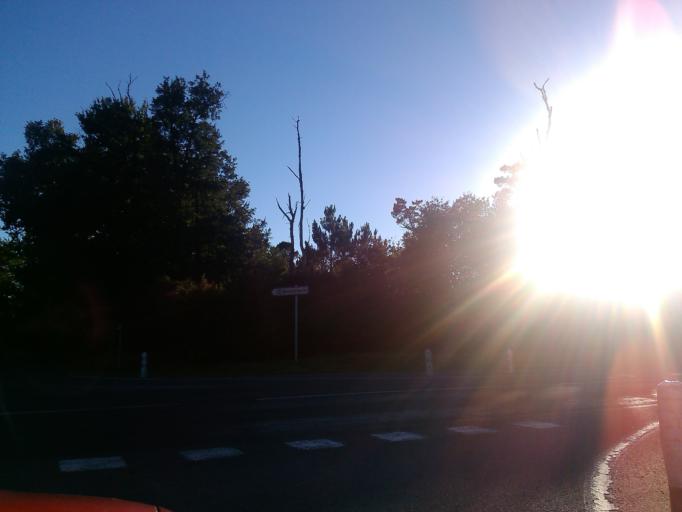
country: FR
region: Poitou-Charentes
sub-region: Departement de la Charente-Maritime
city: Chaillevette
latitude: 45.7191
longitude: -1.0736
